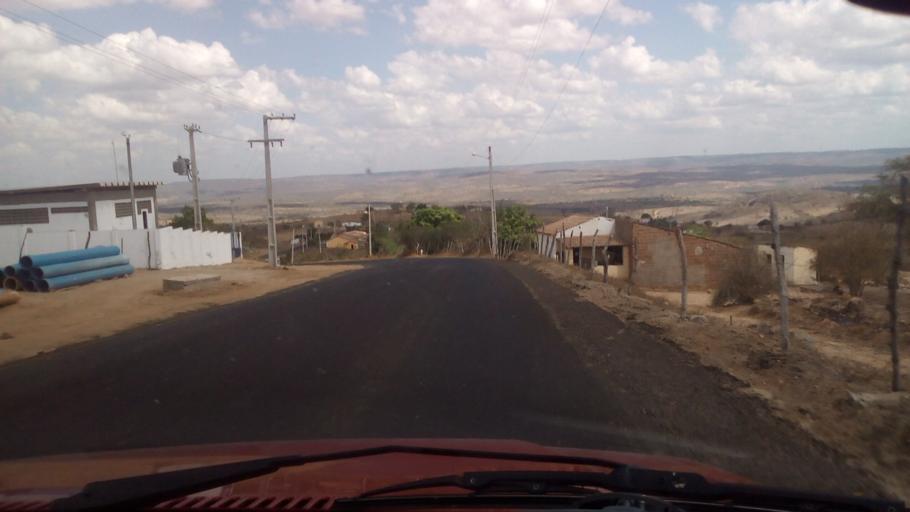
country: BR
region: Paraiba
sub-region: Cacimba De Dentro
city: Cacimba de Dentro
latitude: -6.6518
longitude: -35.7747
